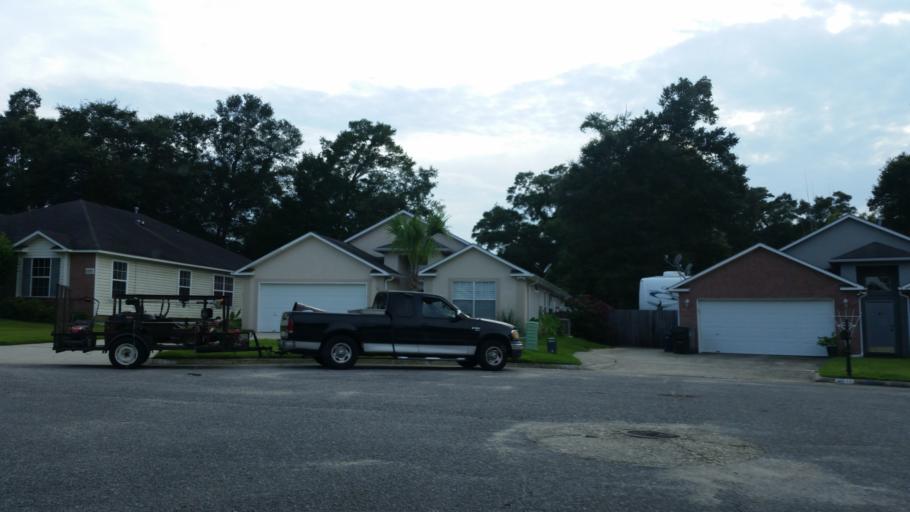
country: US
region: Florida
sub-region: Escambia County
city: Ferry Pass
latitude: 30.5133
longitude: -87.2016
